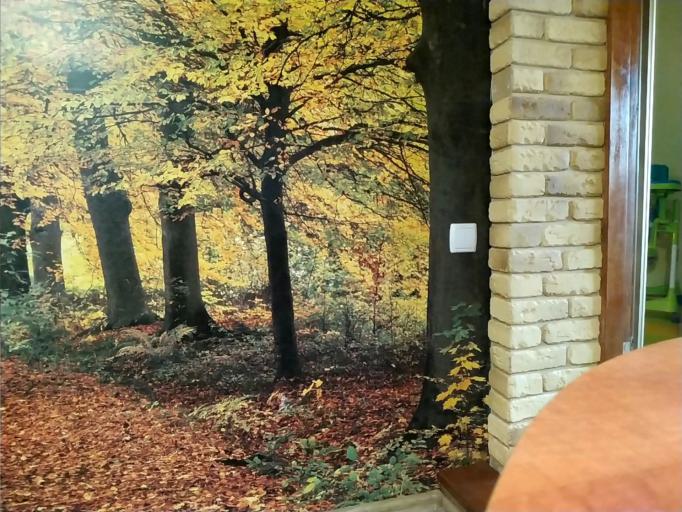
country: RU
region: Leningrad
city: Tolmachevo
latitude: 58.9279
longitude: 29.7287
